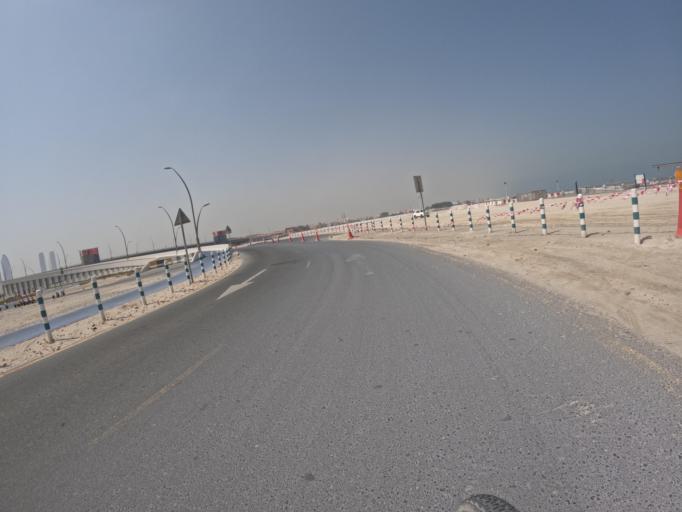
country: AE
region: Dubai
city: Dubai
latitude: 25.1979
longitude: 55.2343
